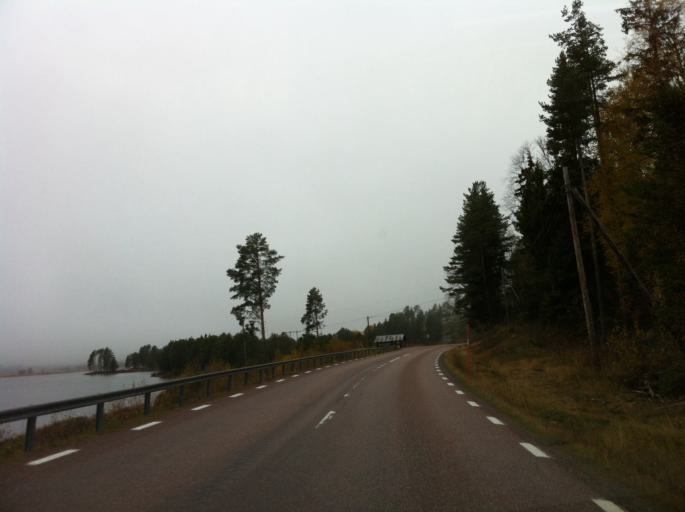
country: NO
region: Hedmark
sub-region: Trysil
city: Innbygda
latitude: 61.8538
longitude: 12.7435
